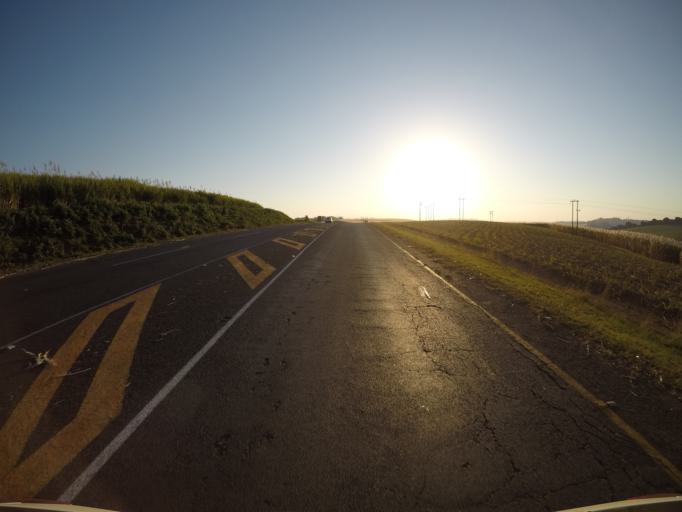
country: ZA
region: KwaZulu-Natal
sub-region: uThungulu District Municipality
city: eSikhawini
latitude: -28.9427
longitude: 31.7377
